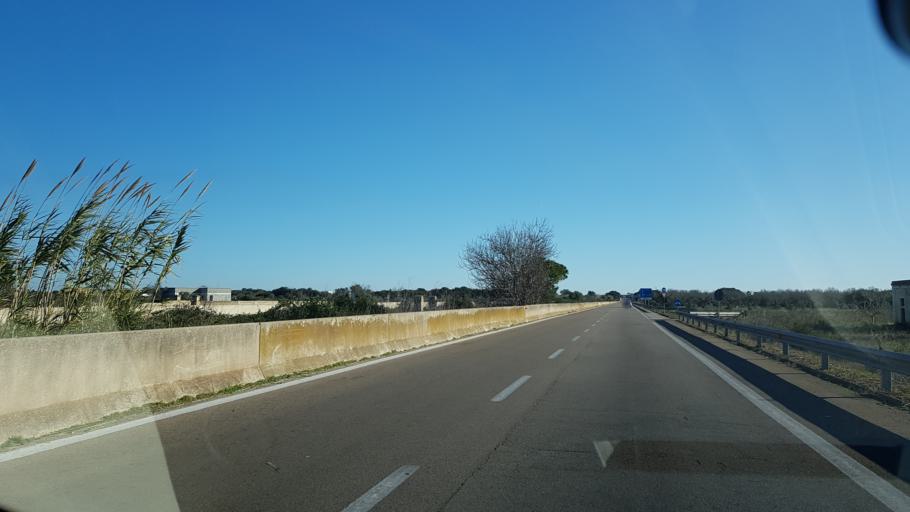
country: IT
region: Apulia
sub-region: Provincia di Lecce
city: Alezio
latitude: 40.0218
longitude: 18.0404
